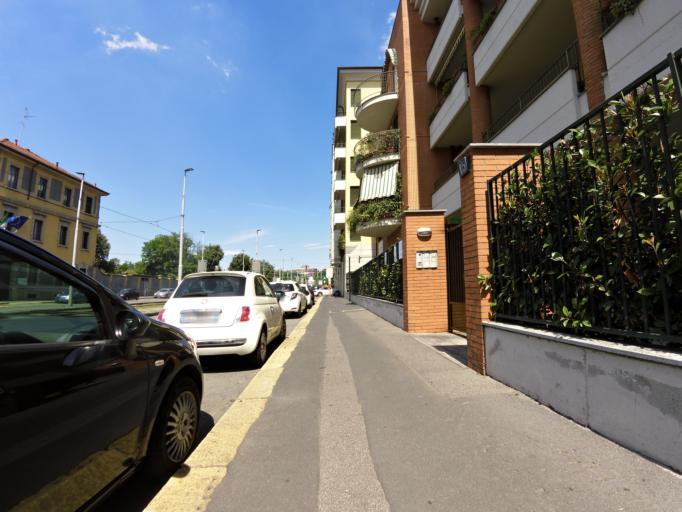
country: IT
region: Lombardy
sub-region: Citta metropolitana di Milano
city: Linate
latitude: 45.4592
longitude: 9.2397
